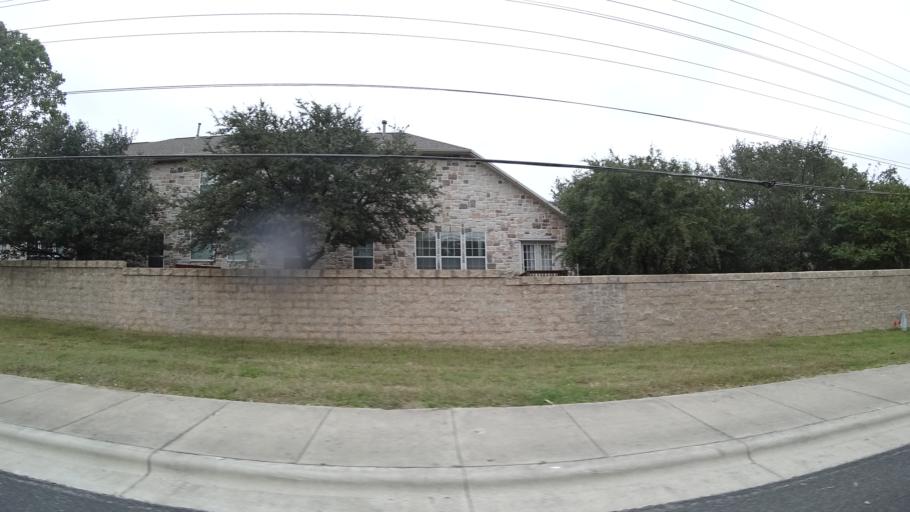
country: US
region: Texas
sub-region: Williamson County
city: Anderson Mill
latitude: 30.4492
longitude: -97.8152
